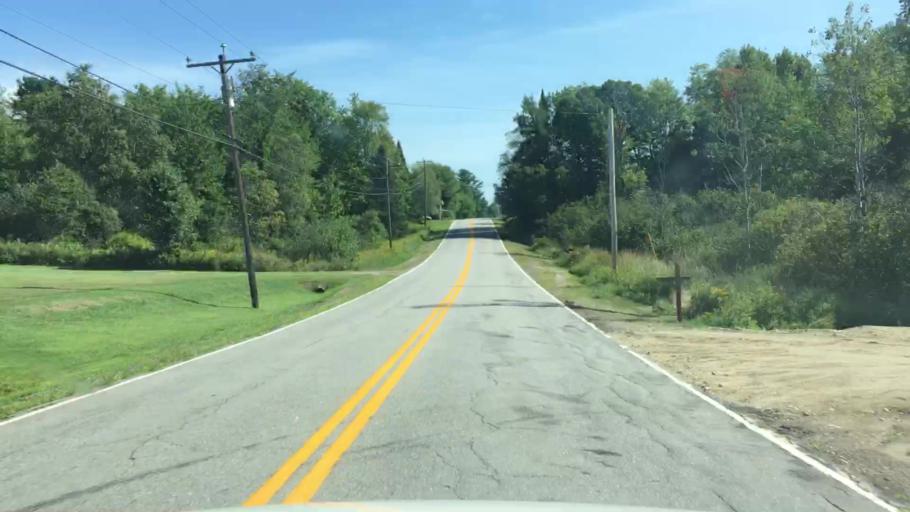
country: US
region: Maine
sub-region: Kennebec County
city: Monmouth
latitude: 44.2117
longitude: -70.0844
